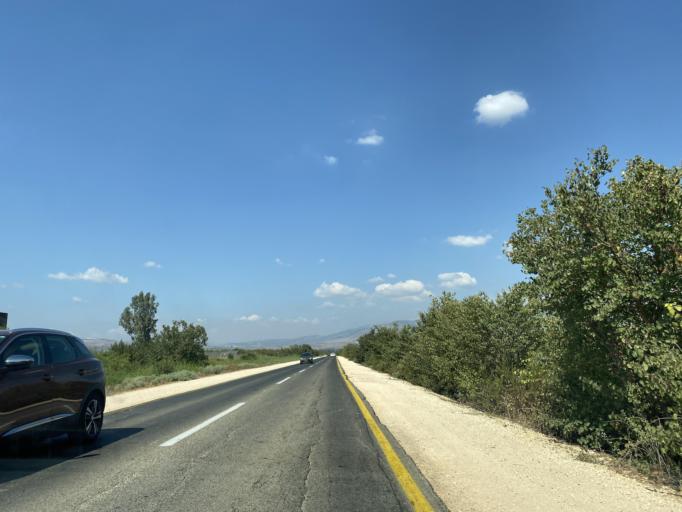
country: IL
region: Northern District
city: Qiryat Shemona
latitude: 33.1672
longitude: 35.5974
